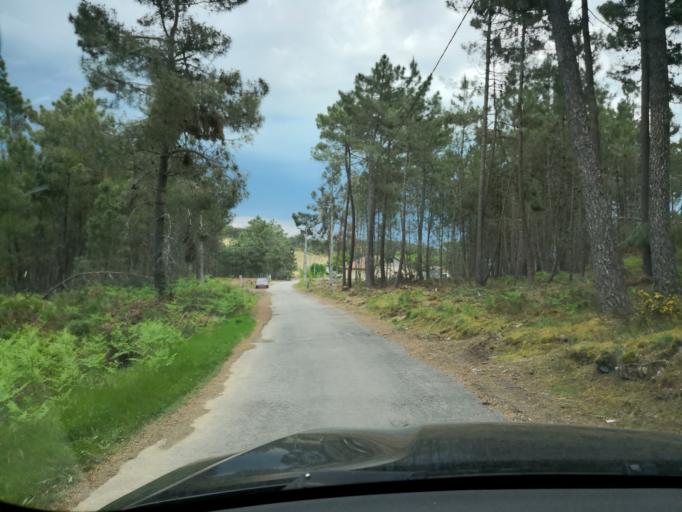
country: PT
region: Vila Real
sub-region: Sabrosa
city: Vilela
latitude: 41.2434
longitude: -7.6636
